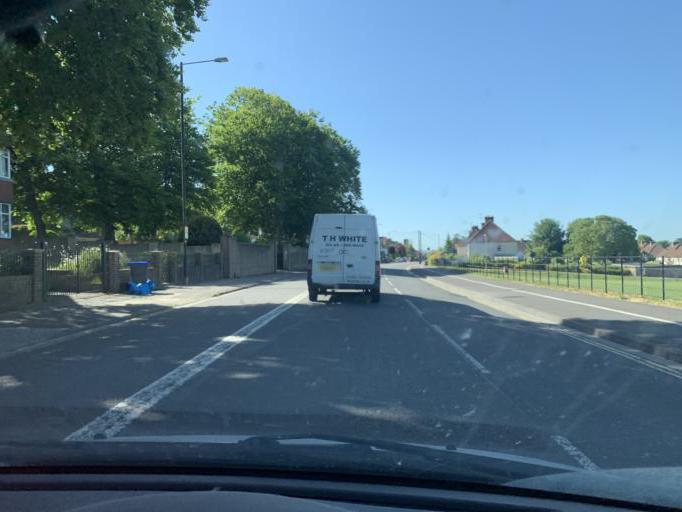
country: GB
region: England
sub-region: Wiltshire
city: Salisbury
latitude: 51.0866
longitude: -1.7980
